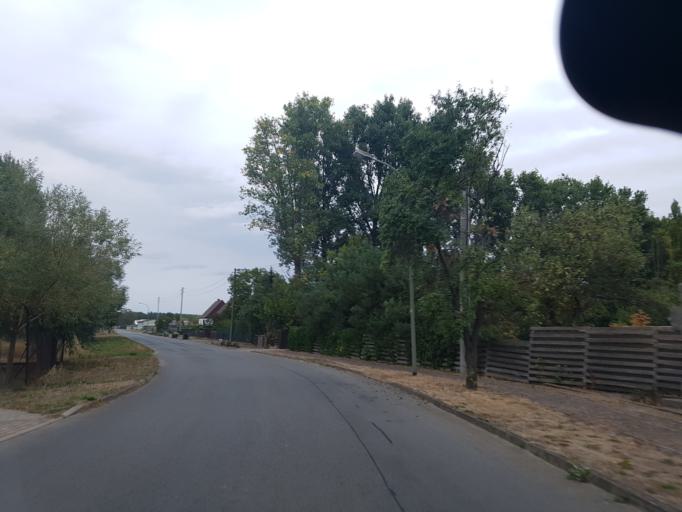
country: DE
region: Saxony-Anhalt
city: Prettin
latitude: 51.7030
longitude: 12.9006
